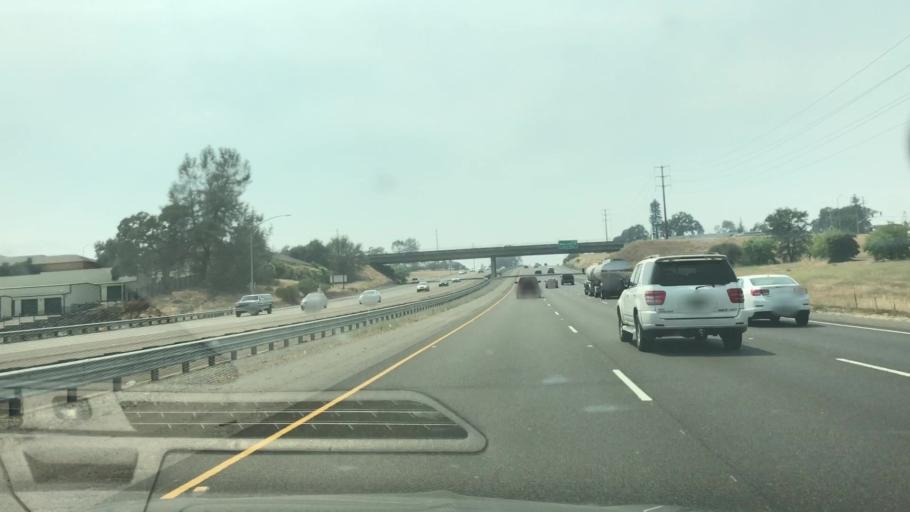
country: US
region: California
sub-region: El Dorado County
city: Cameron Park
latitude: 38.6571
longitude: -120.9958
